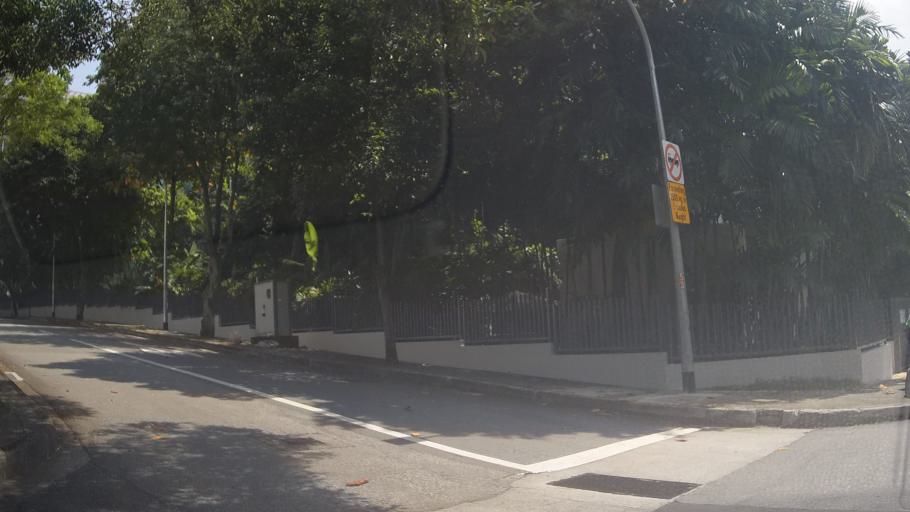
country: SG
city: Singapore
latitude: 1.3237
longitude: 103.8005
